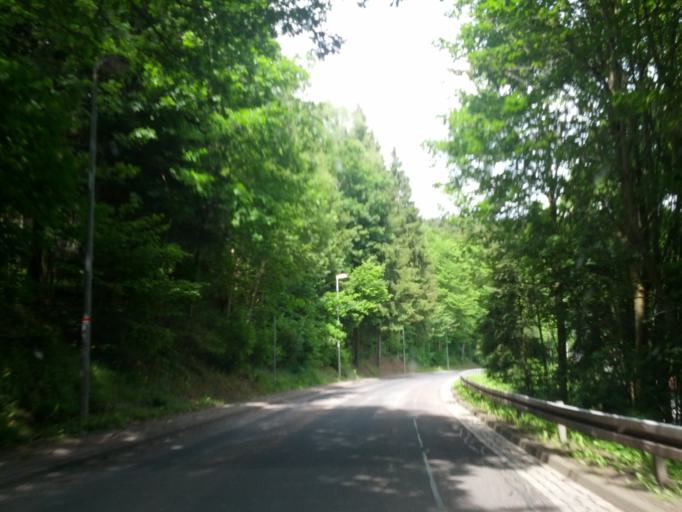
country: DE
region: Thuringia
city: Finsterbergen
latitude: 50.8385
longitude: 10.5961
